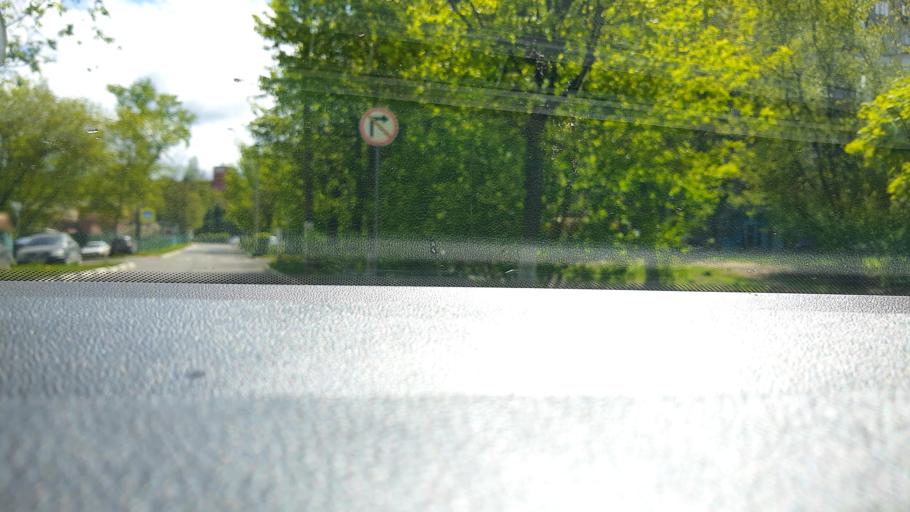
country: RU
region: Moskovskaya
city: Dmitrov
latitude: 56.3496
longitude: 37.5297
